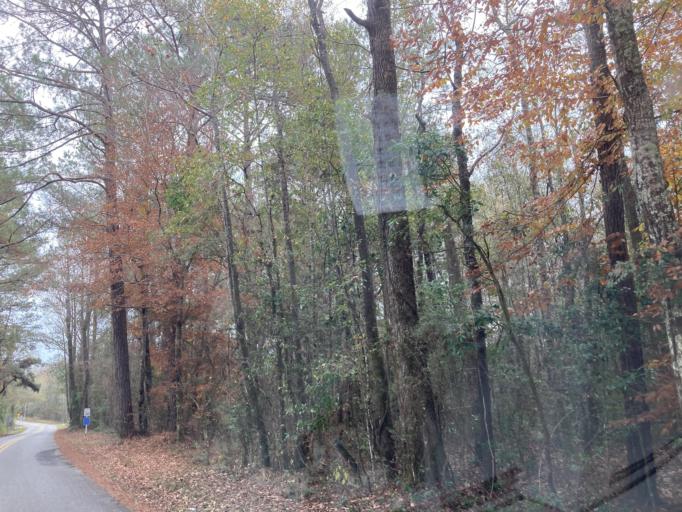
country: US
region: Mississippi
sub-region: Stone County
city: Wiggins
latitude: 31.0587
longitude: -89.2052
